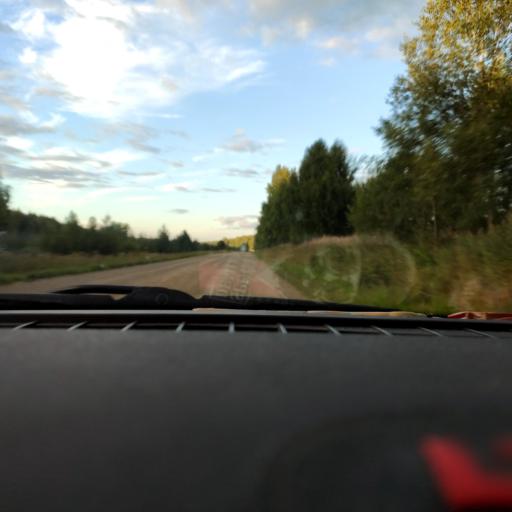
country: RU
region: Perm
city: Pavlovskiy
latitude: 57.9925
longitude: 54.8839
